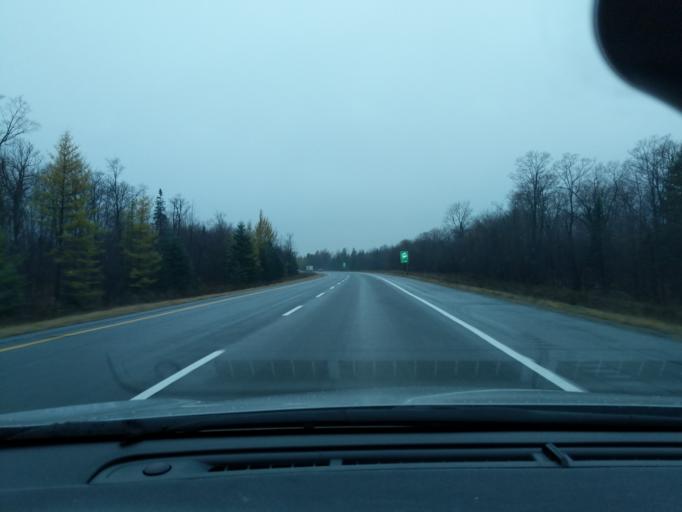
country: CA
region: Quebec
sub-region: Capitale-Nationale
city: Saint-Marc-des-Carrieres
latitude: 46.6579
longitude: -71.9692
